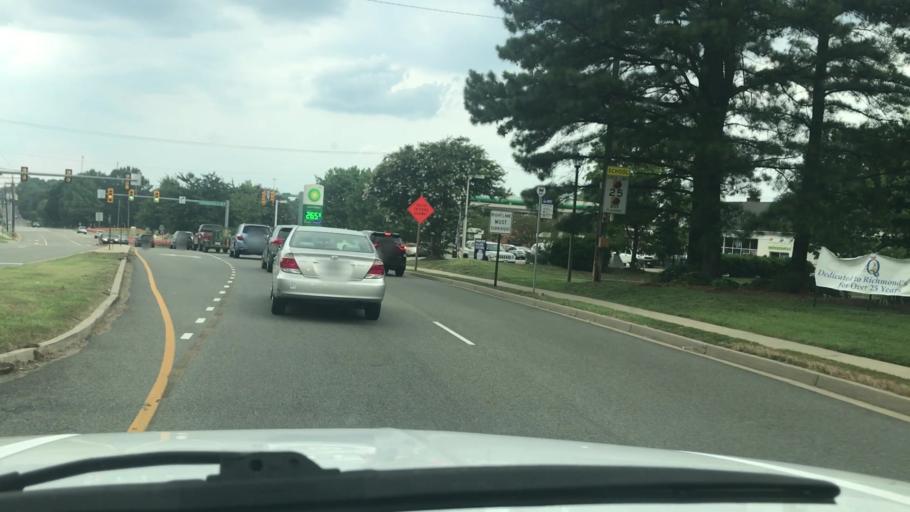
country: US
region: Virginia
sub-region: Henrico County
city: Tuckahoe
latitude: 37.6072
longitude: -77.5775
